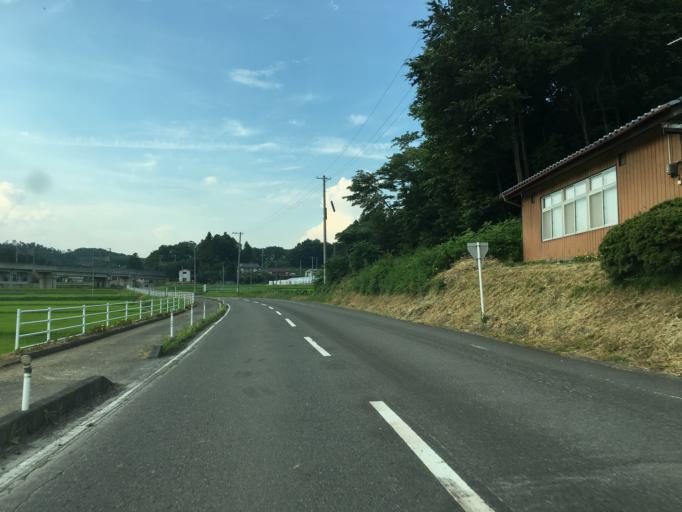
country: JP
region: Fukushima
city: Motomiya
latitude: 37.5314
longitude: 140.4431
